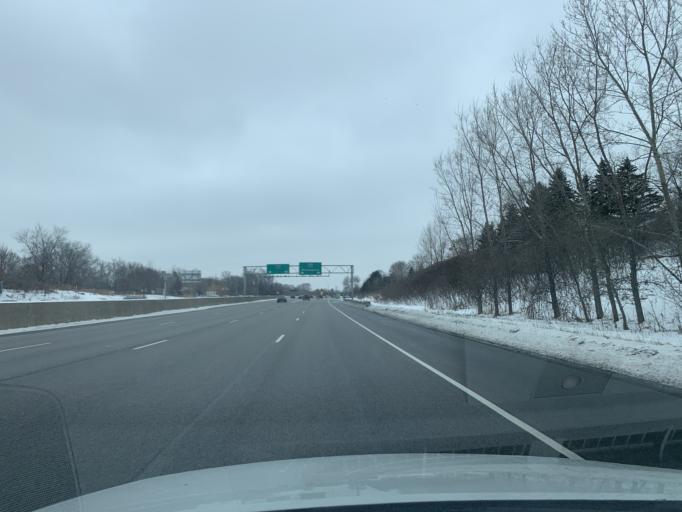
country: US
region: Minnesota
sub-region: Anoka County
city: Coon Rapids
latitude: 45.1275
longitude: -93.3005
